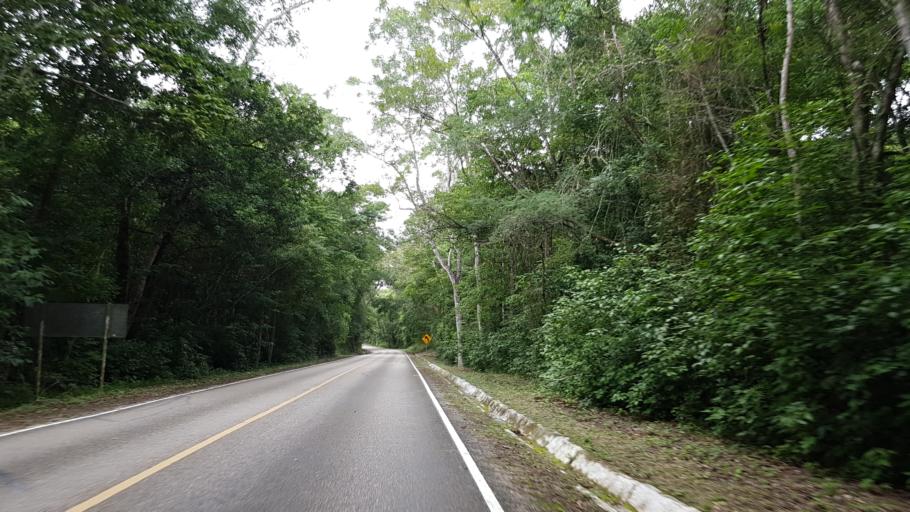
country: GT
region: Peten
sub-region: Municipio de San Jose
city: San Jose
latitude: 17.2167
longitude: -89.6117
